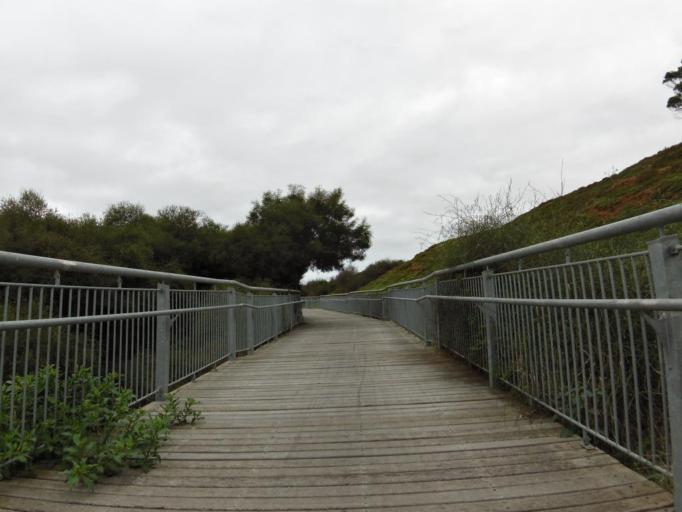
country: AU
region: Victoria
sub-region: Wyndham
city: Werribee
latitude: -37.9340
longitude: 144.6593
